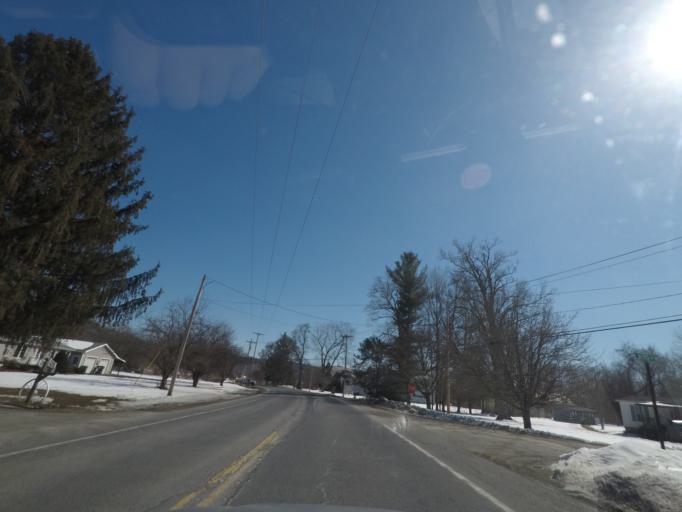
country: US
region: New York
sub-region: Saratoga County
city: Stillwater
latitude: 42.9246
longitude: -73.6403
